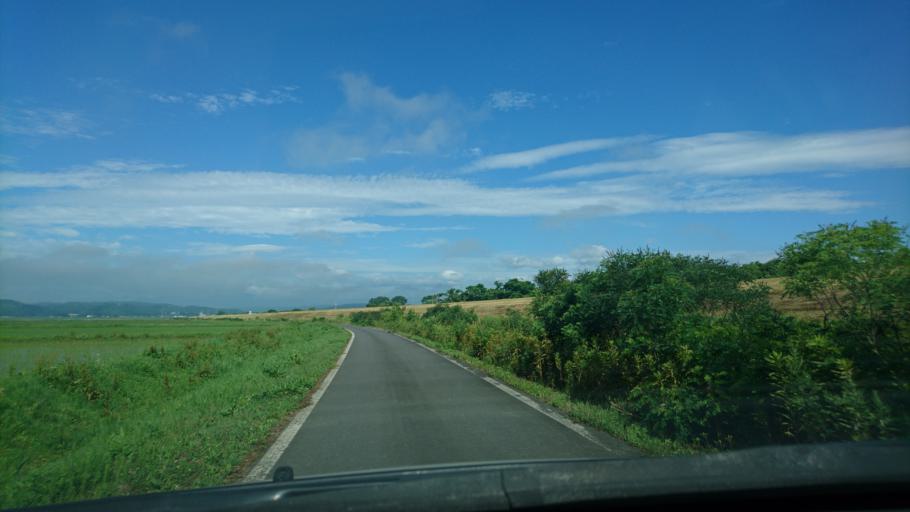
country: JP
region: Iwate
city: Ichinoseki
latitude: 38.9742
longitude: 141.1514
